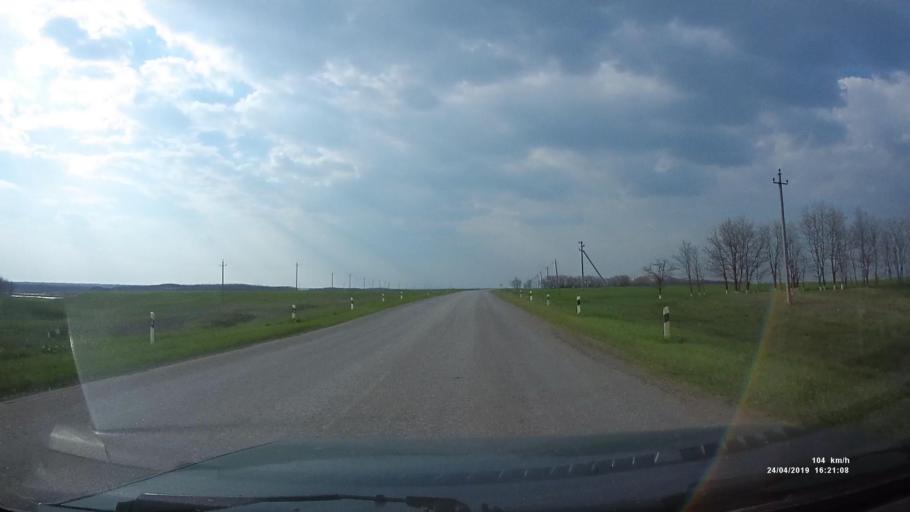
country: RU
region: Rostov
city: Orlovskiy
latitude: 46.8009
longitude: 42.0688
